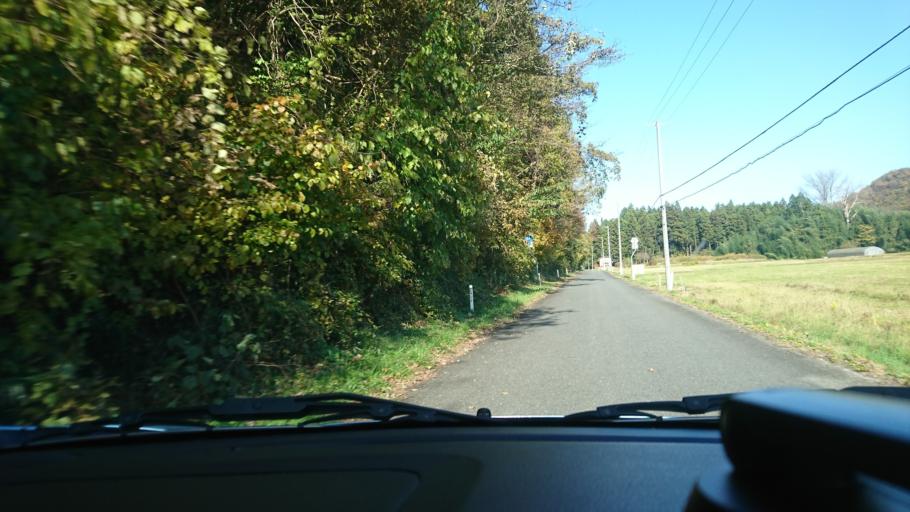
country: JP
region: Iwate
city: Ichinoseki
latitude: 38.8147
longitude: 141.2496
